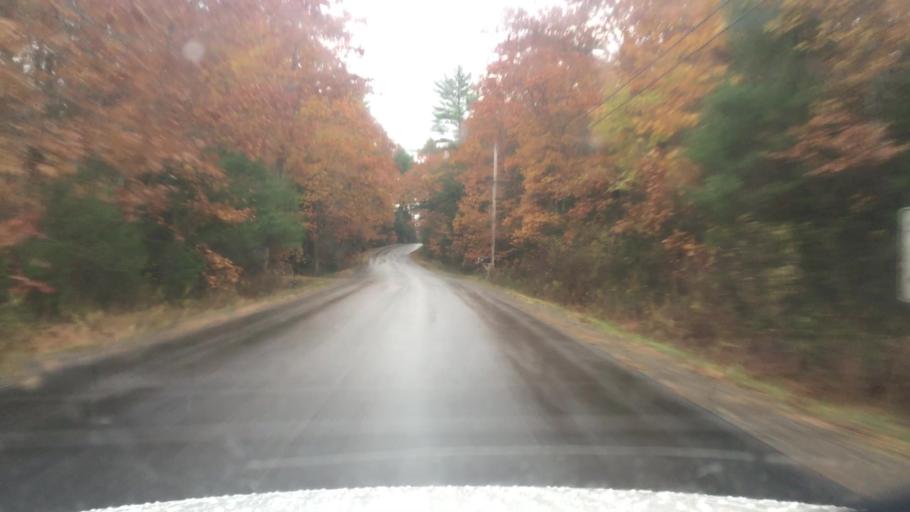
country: US
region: Maine
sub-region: Waldo County
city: Lincolnville
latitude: 44.3137
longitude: -69.0714
